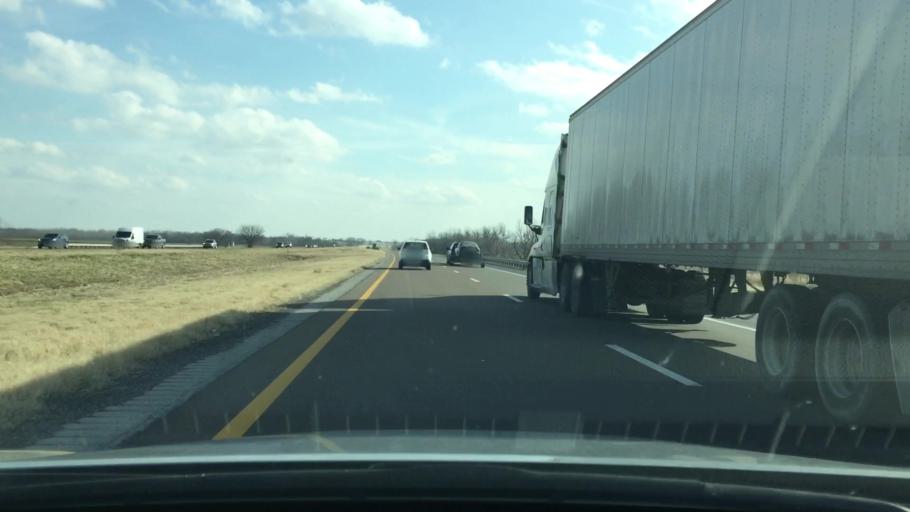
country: US
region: Oklahoma
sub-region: Garvin County
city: Pauls Valley
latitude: 34.7949
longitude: -97.3012
